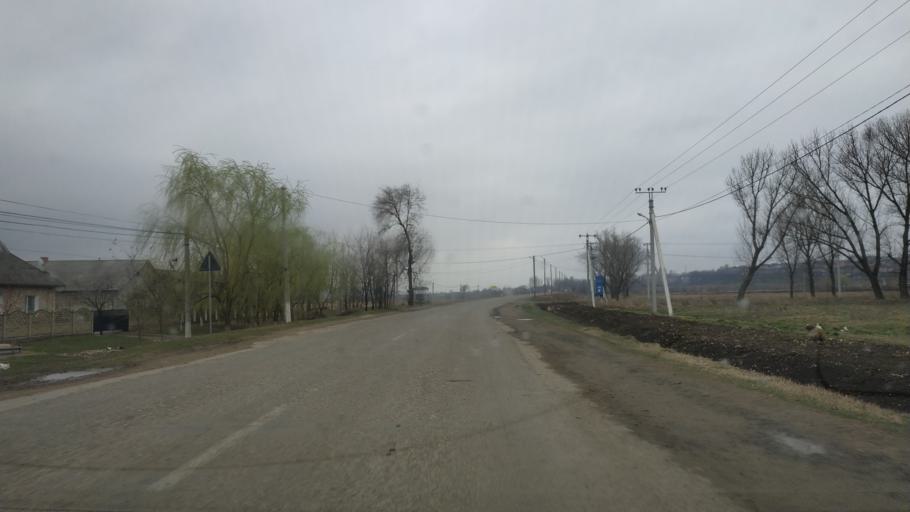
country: MD
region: Cantemir
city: Iargara
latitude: 46.3610
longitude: 28.3388
